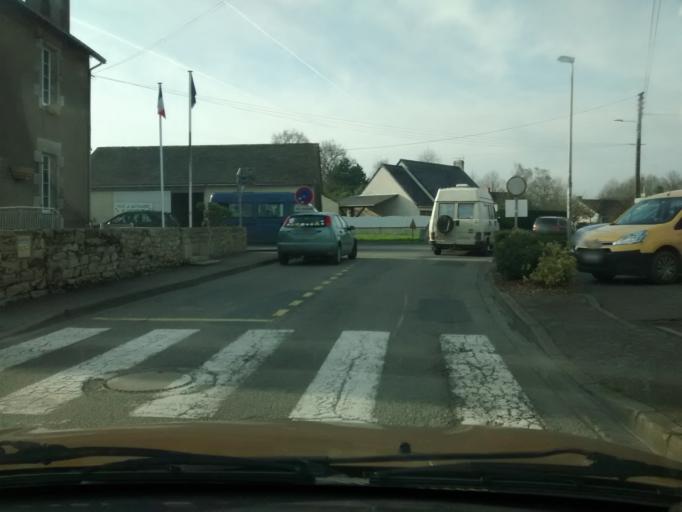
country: FR
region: Pays de la Loire
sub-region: Departement de la Loire-Atlantique
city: Notre-Dame-des-Landes
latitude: 47.3806
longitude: -1.7115
